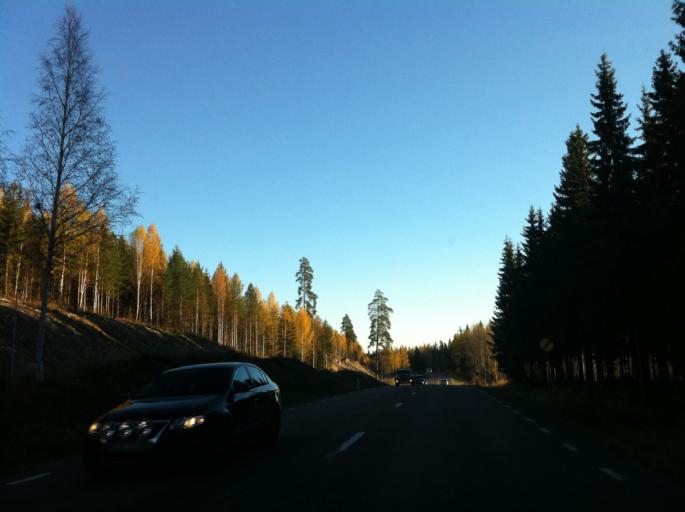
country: SE
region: Dalarna
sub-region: Faluns Kommun
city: Grycksbo
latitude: 60.6772
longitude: 15.5091
